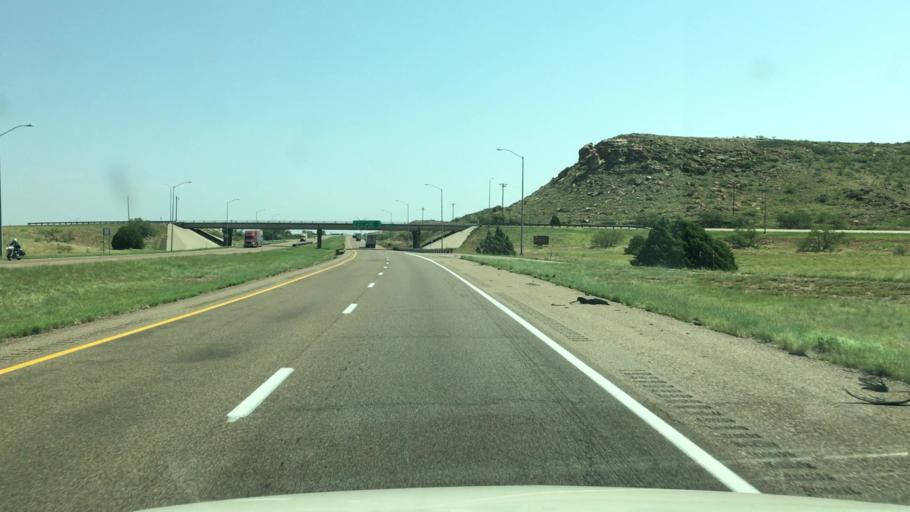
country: US
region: New Mexico
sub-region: Quay County
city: Tucumcari
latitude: 35.1504
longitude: -103.7780
